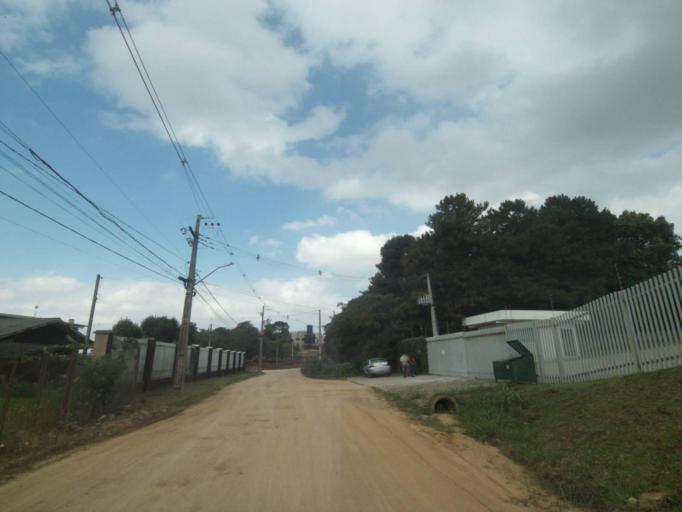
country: BR
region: Parana
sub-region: Araucaria
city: Araucaria
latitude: -25.5166
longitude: -49.3452
